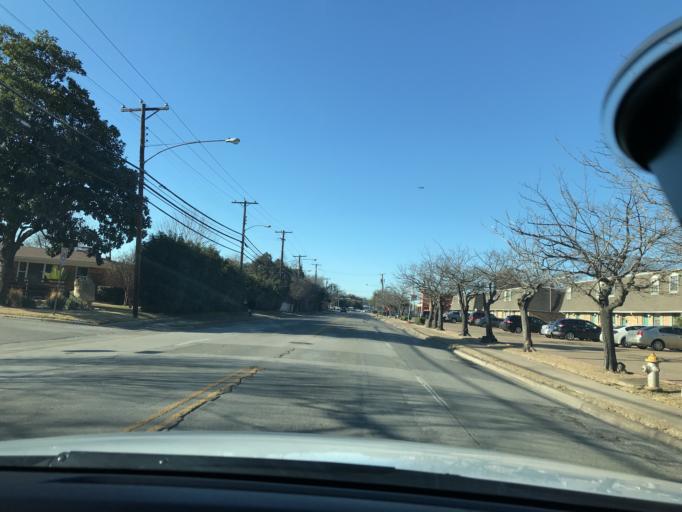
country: US
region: Texas
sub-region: Dallas County
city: Garland
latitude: 32.8365
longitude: -96.6942
